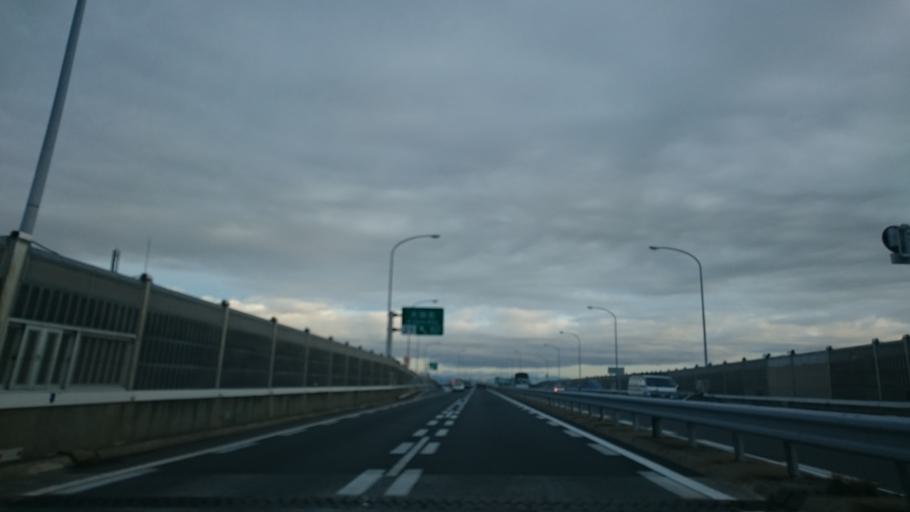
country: JP
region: Aichi
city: Kanie
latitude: 35.1776
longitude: 136.8162
